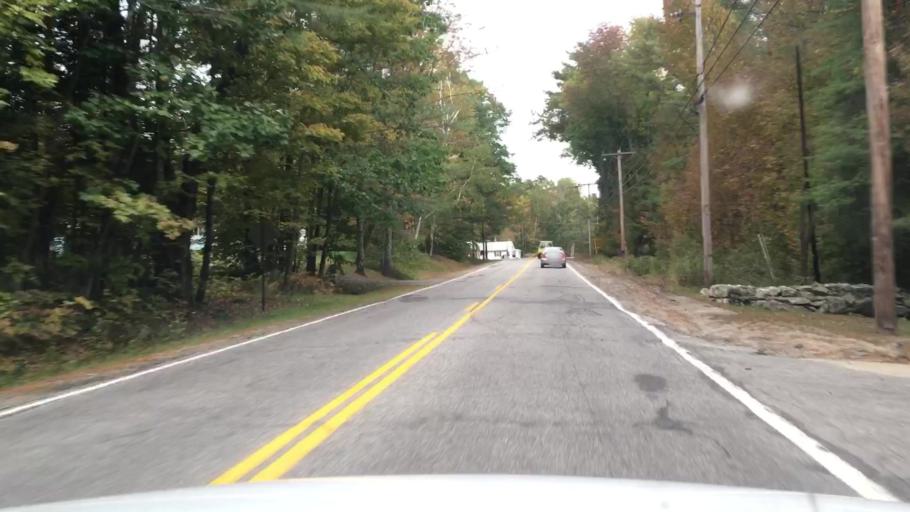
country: US
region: Maine
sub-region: Oxford County
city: Norway
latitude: 44.2161
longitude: -70.5821
